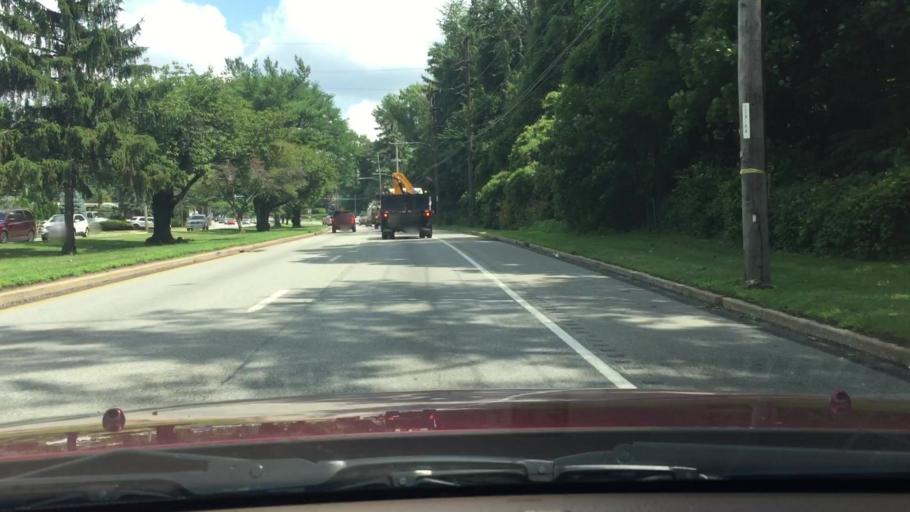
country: US
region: Pennsylvania
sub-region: Delaware County
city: Broomall
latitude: 39.9750
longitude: -75.3294
